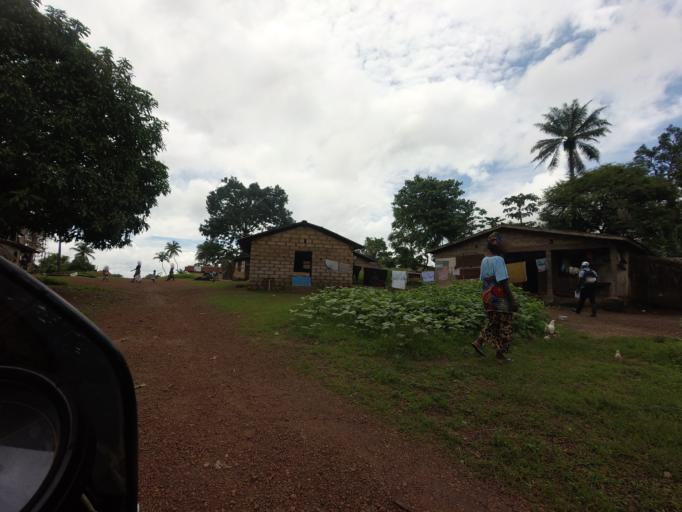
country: SL
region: Northern Province
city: Mambolo
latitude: 8.9720
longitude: -12.9986
